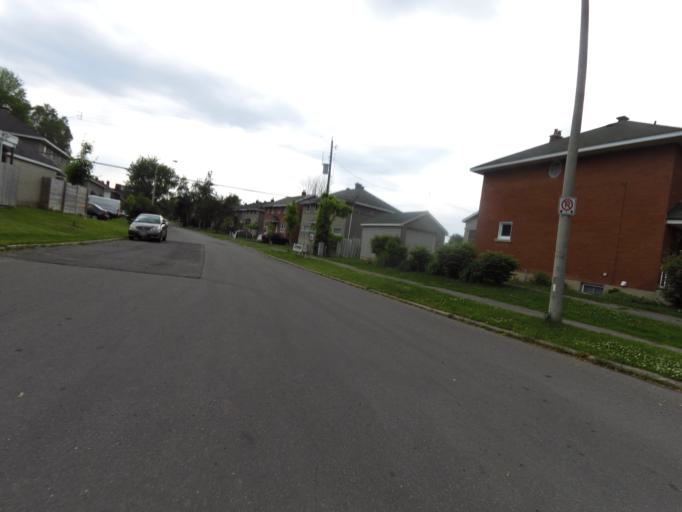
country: CA
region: Ontario
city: Ottawa
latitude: 45.3794
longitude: -75.7235
